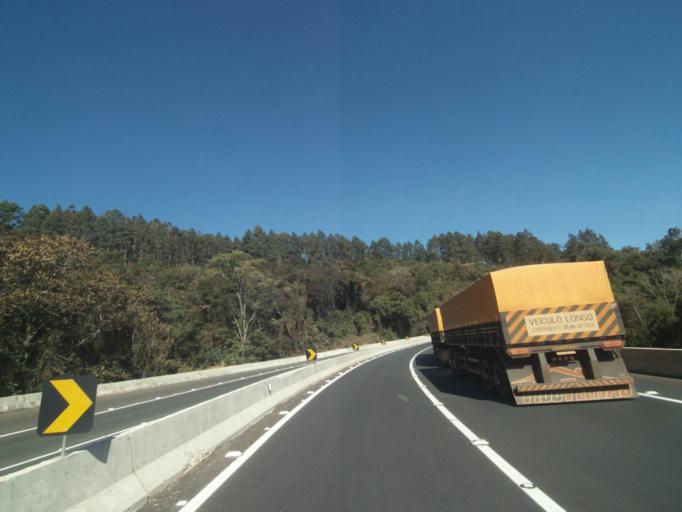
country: BR
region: Parana
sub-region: Tibagi
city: Tibagi
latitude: -24.8053
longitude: -50.4886
